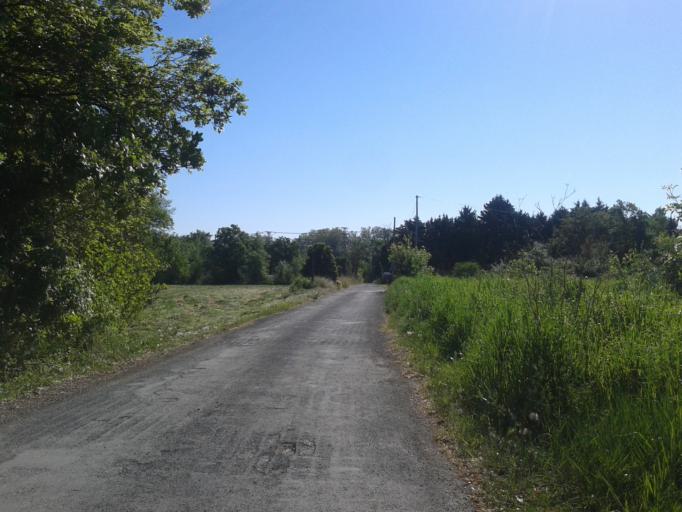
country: FR
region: Languedoc-Roussillon
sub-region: Departement des Pyrenees-Orientales
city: Toulouges
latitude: 42.6743
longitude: 2.8136
